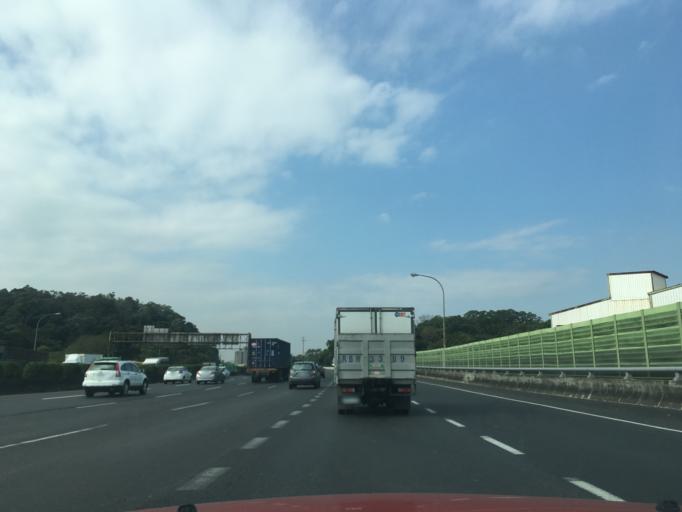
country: TW
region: Taipei
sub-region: Taipei
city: Banqiao
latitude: 24.9597
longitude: 121.4279
